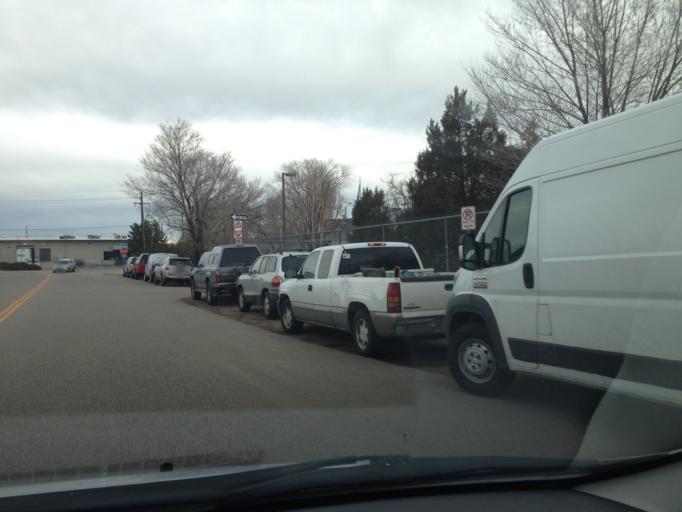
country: US
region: Colorado
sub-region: Boulder County
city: Boulder
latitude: 40.0184
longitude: -105.2455
